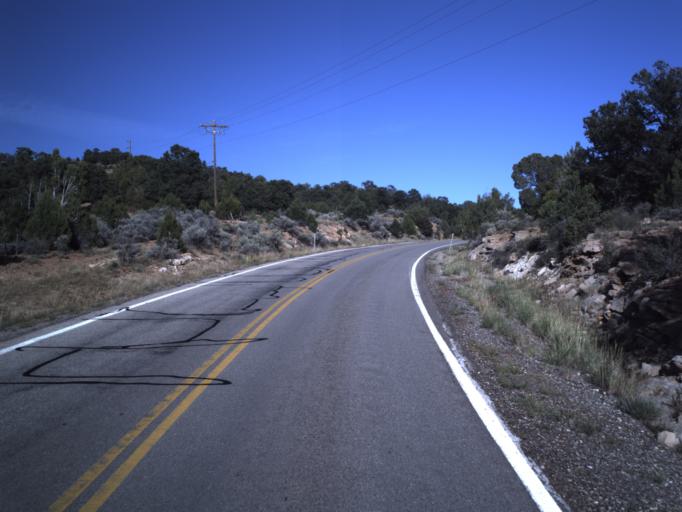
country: US
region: Utah
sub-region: Grand County
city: Moab
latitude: 38.3160
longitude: -109.2358
